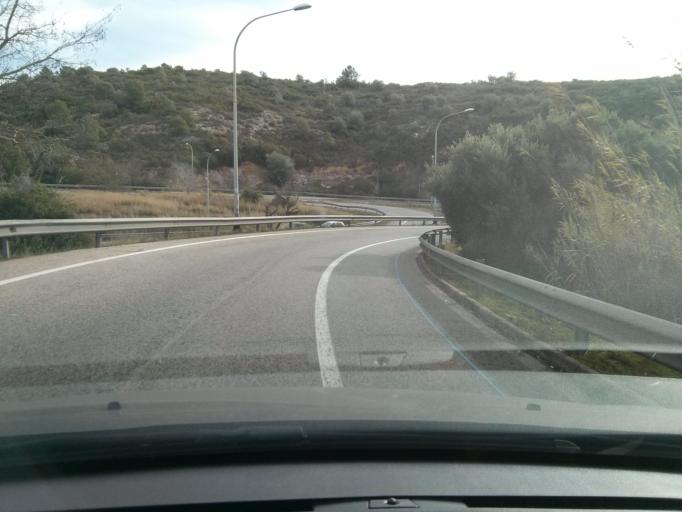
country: ES
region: Catalonia
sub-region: Provincia de Tarragona
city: Tarragona
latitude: 41.1409
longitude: 1.2385
